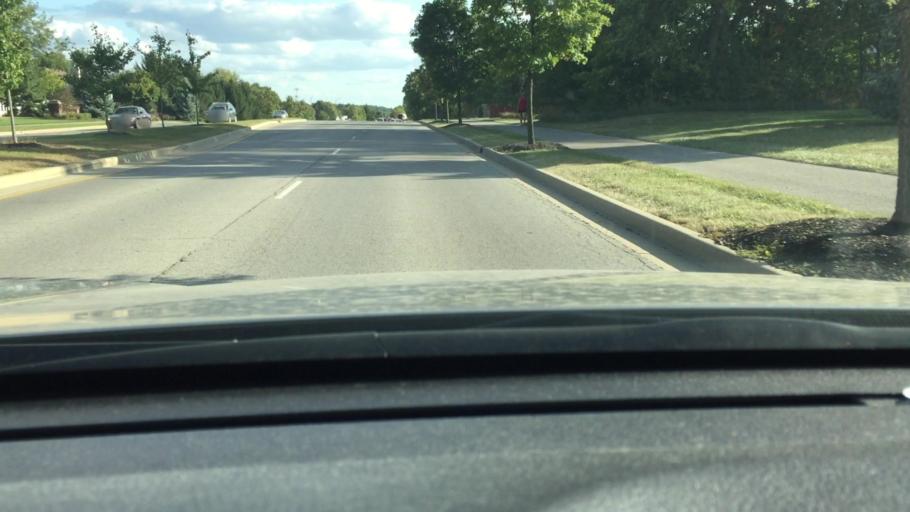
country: US
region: Indiana
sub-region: Hamilton County
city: Carmel
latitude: 39.9826
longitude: -86.0706
